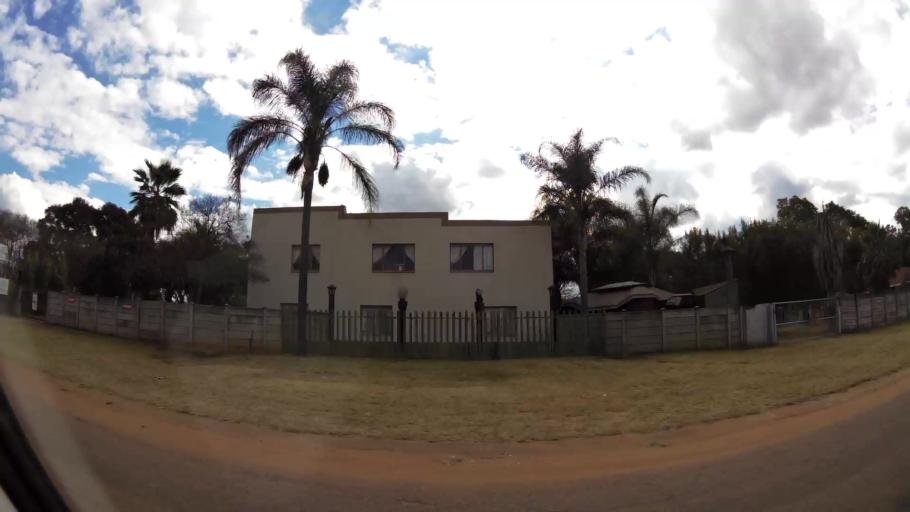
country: ZA
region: Limpopo
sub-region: Waterberg District Municipality
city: Modimolle
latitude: -24.7105
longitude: 28.4039
